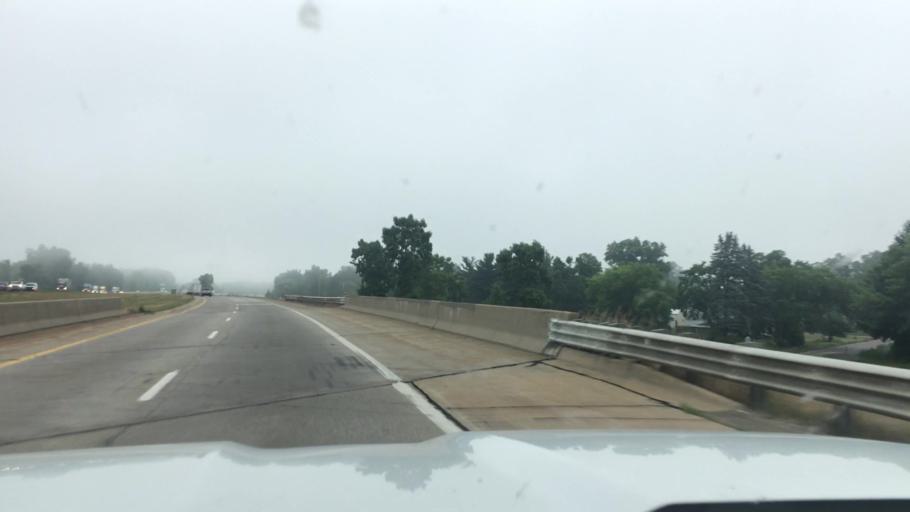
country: US
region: Michigan
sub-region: Shiawassee County
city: Perry
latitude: 42.8194
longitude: -84.2709
